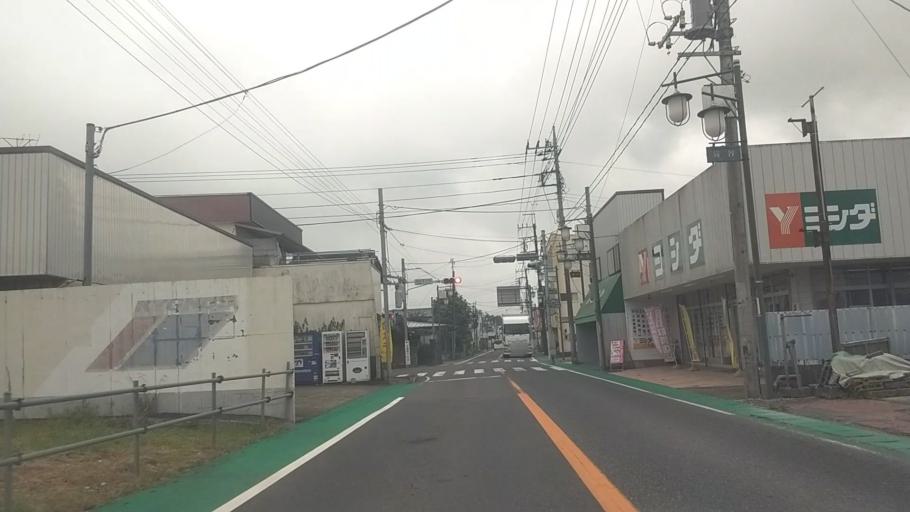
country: JP
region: Chiba
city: Ohara
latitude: 35.2811
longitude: 140.3102
